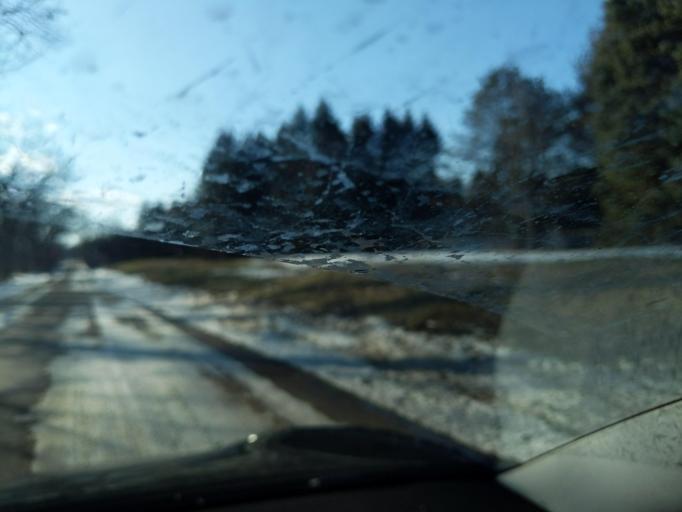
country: US
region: Michigan
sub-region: Ingham County
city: Stockbridge
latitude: 42.5242
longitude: -84.1234
